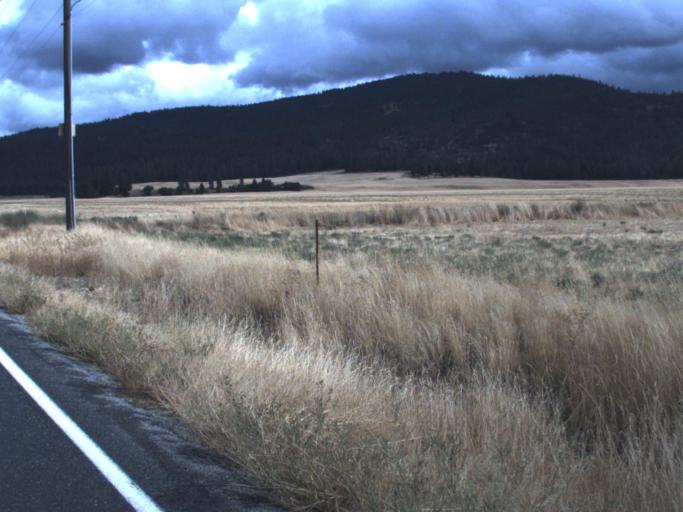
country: US
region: Washington
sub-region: Spokane County
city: Deer Park
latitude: 47.9150
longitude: -117.7980
